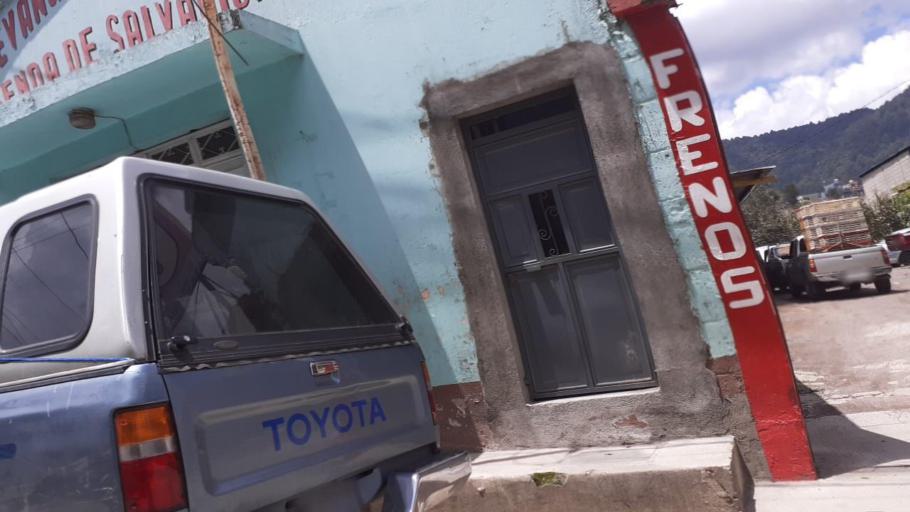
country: GT
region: Quetzaltenango
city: Ostuncalco
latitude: 14.8659
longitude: -91.6248
